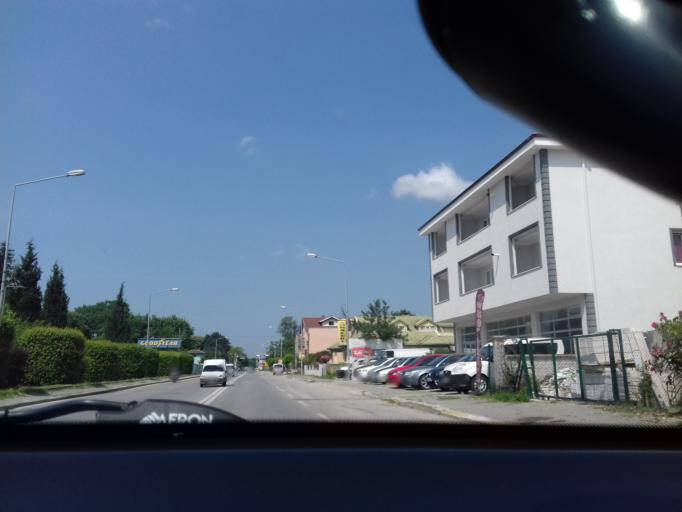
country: TR
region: Sakarya
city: Adapazari
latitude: 40.7266
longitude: 30.3746
